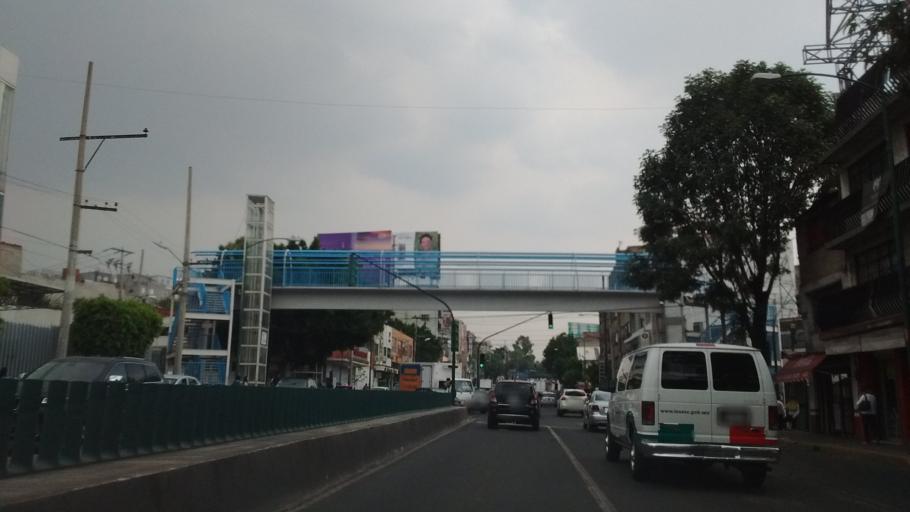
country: MX
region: Mexico City
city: Polanco
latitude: 19.4088
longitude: -99.1901
